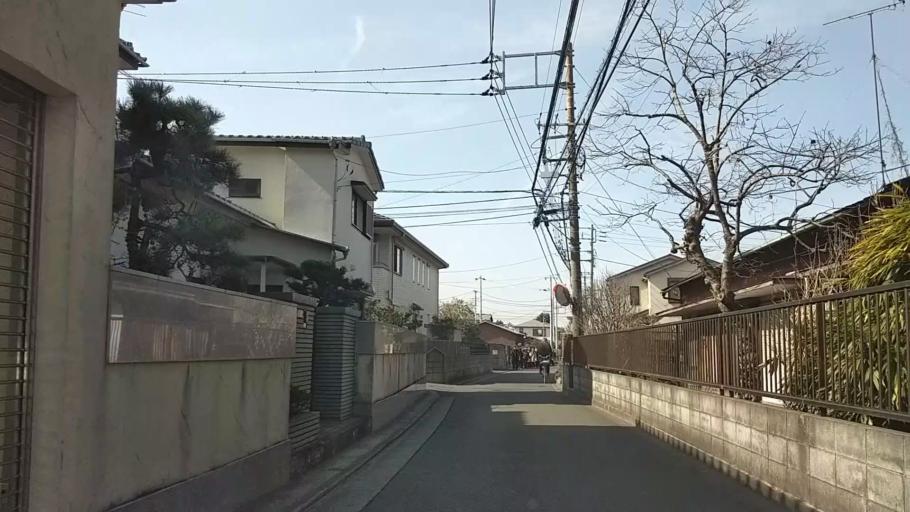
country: JP
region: Kanagawa
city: Chigasaki
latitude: 35.3482
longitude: 139.4183
